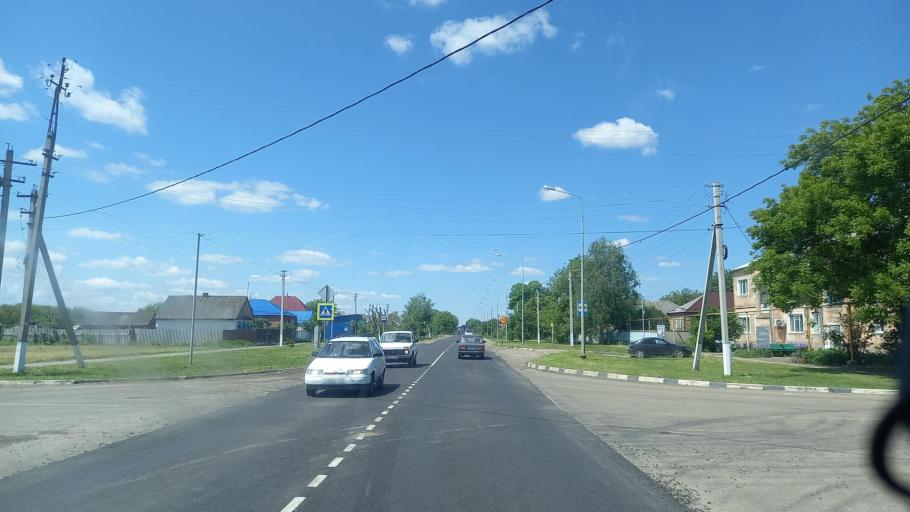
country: RU
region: Krasnodarskiy
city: Tbilisskaya
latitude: 45.3264
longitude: 40.2530
